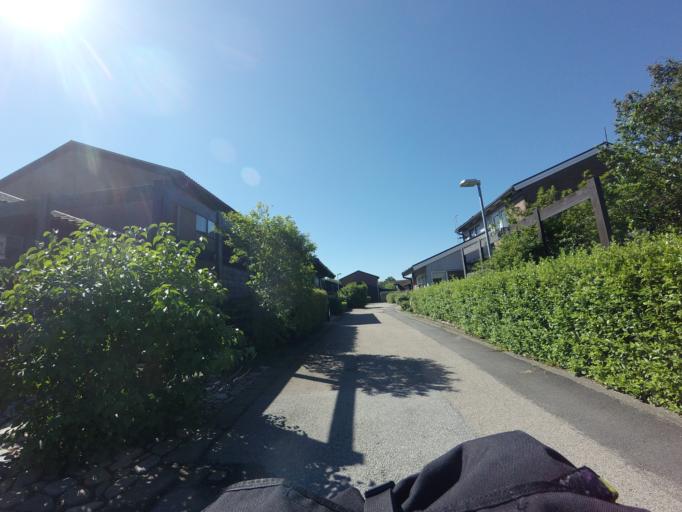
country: SE
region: Skane
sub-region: Hoganas Kommun
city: Hoganas
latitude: 56.1740
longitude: 12.5670
